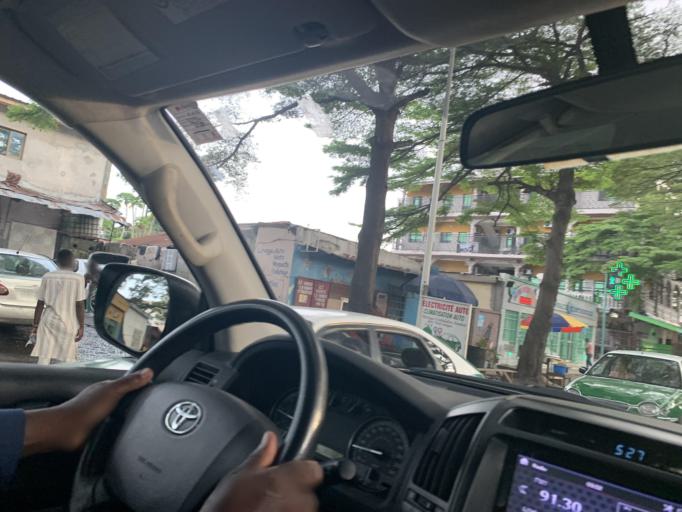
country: CG
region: Brazzaville
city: Brazzaville
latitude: -4.2631
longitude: 15.2891
